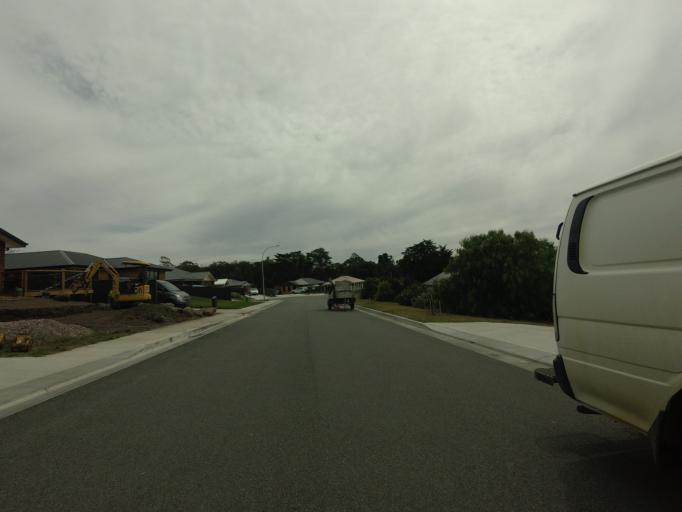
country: AU
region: Tasmania
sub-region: Sorell
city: Sorell
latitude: -42.7915
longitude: 147.5297
